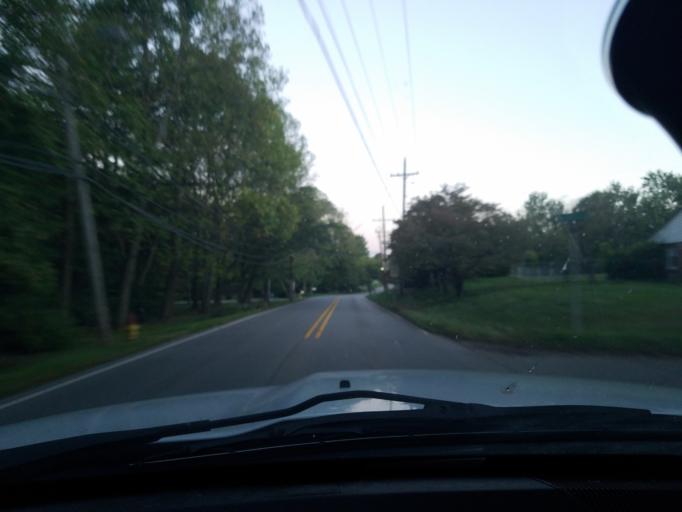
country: US
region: Indiana
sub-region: Floyd County
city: New Albany
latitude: 38.3279
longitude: -85.8038
